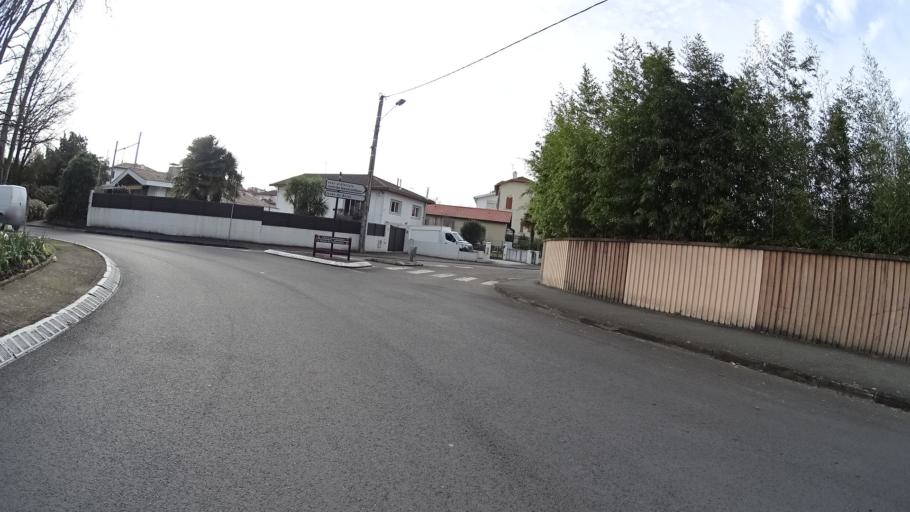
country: FR
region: Aquitaine
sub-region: Departement des Landes
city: Dax
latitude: 43.6998
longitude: -1.0549
